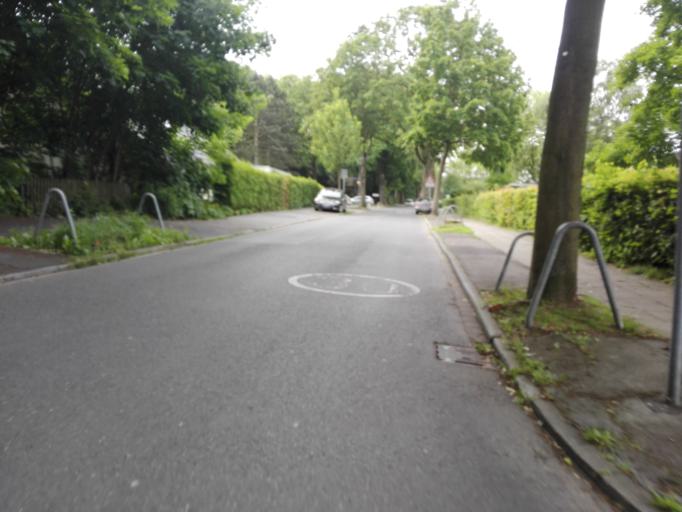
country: DE
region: North Rhine-Westphalia
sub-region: Regierungsbezirk Arnsberg
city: Unna
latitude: 51.5279
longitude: 7.7009
